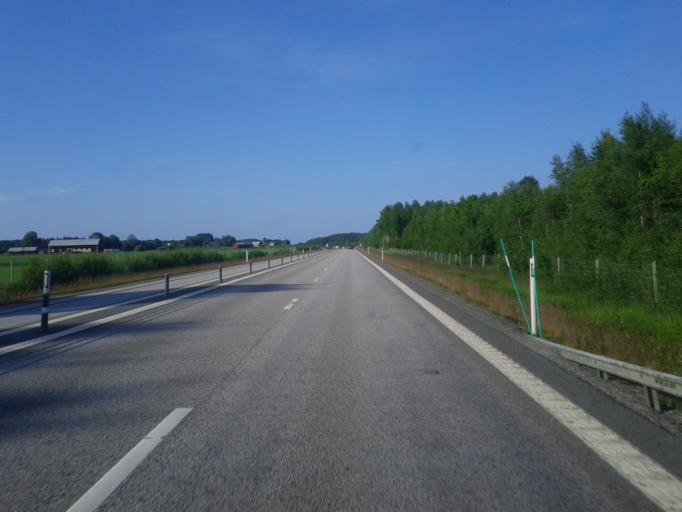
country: SE
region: Vaesterbotten
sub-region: Robertsfors Kommun
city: Robertsfors
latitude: 64.1473
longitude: 20.9026
